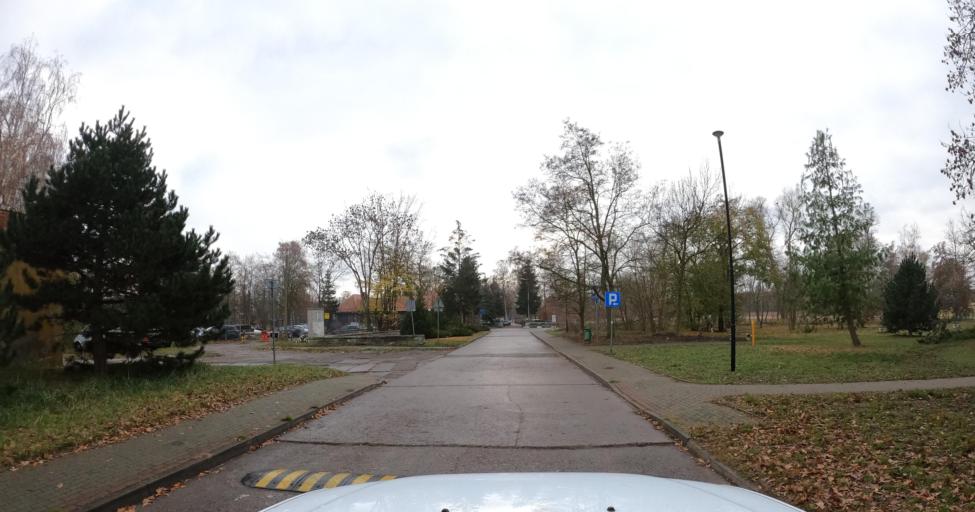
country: PL
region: West Pomeranian Voivodeship
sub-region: Powiat kamienski
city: Dziwnow
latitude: 54.0173
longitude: 14.7475
